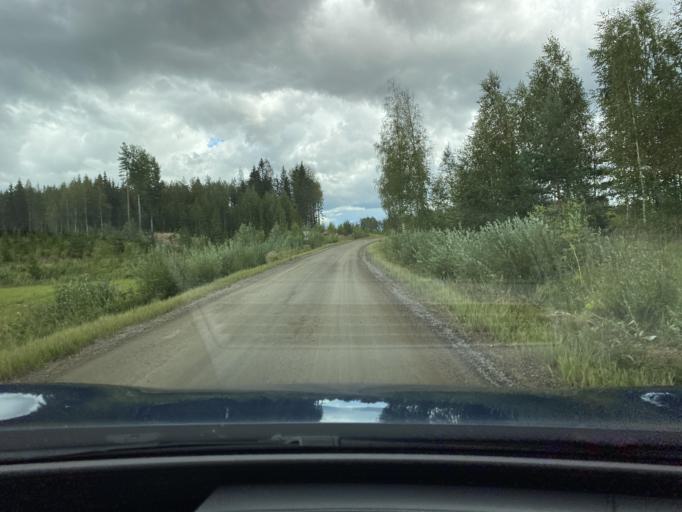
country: FI
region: Pirkanmaa
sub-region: Lounais-Pirkanmaa
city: Punkalaidun
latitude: 61.2316
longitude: 23.1495
